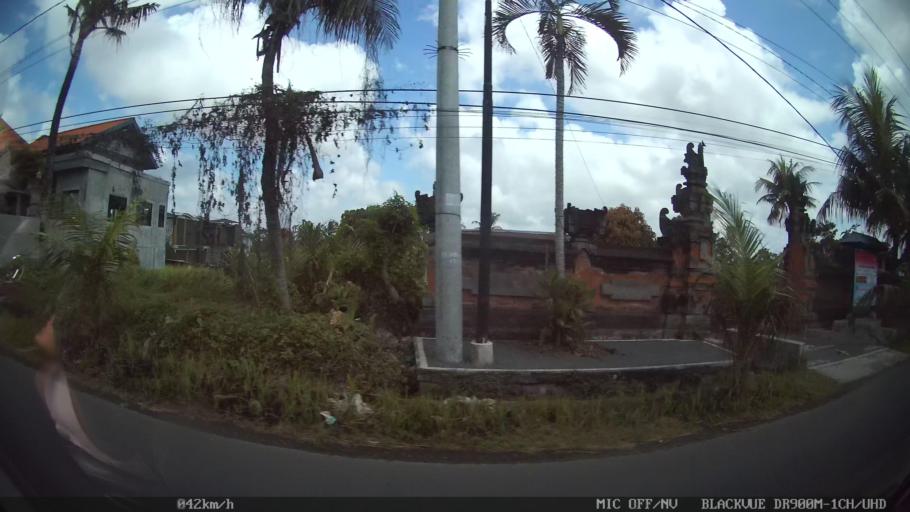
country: ID
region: Bali
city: Banjar Desa
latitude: -8.5724
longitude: 115.2865
